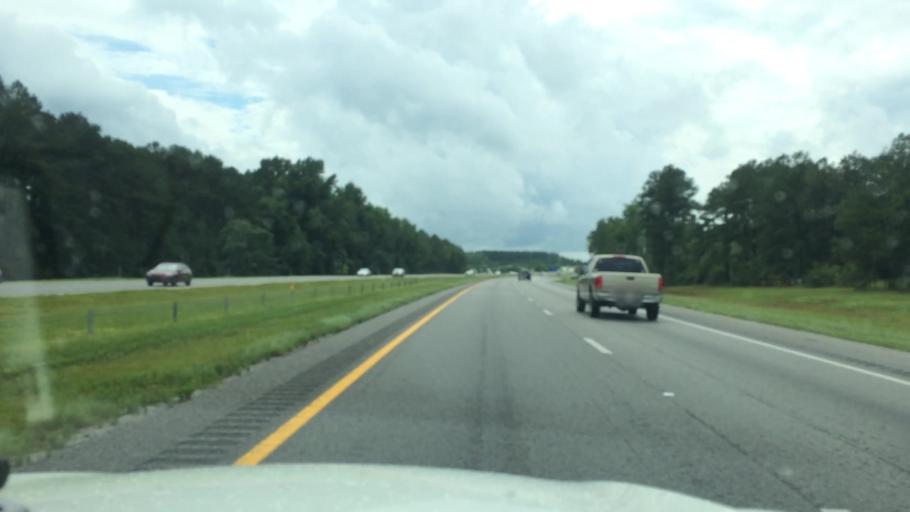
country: US
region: South Carolina
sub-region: Kershaw County
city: Lugoff
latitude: 34.2053
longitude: -80.6535
